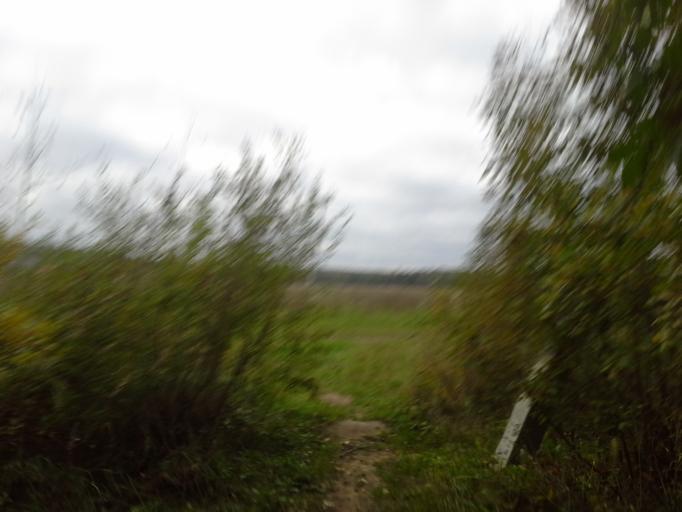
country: RU
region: Moskovskaya
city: Kokoshkino
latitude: 55.6070
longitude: 37.1556
